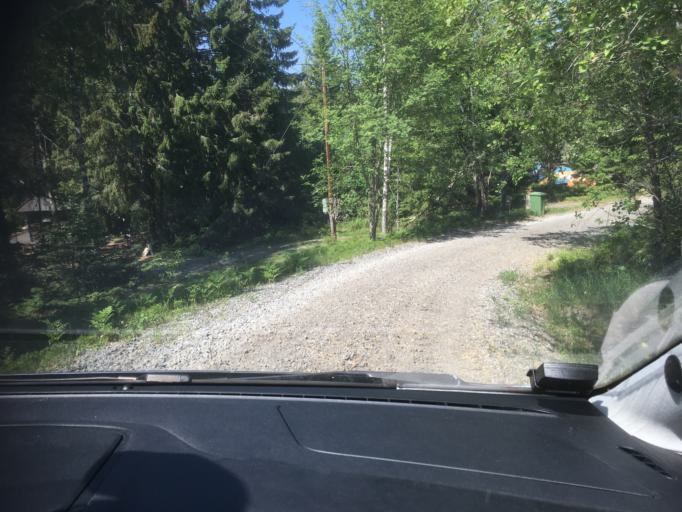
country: SE
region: Stockholm
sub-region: Haninge Kommun
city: Jordbro
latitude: 59.0113
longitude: 18.1635
